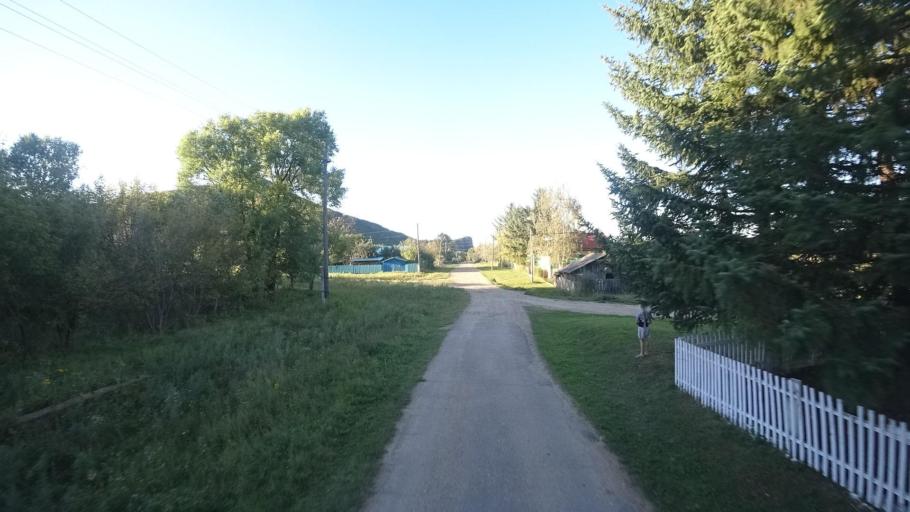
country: RU
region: Primorskiy
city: Kirovskiy
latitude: 44.8314
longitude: 133.5754
